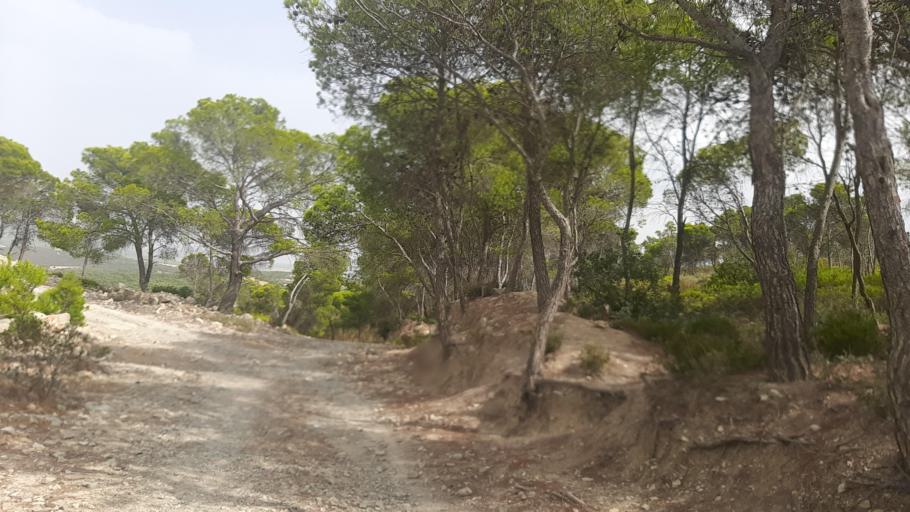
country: TN
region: Zaghwan
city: El Fahs
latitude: 36.1954
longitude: 9.8533
